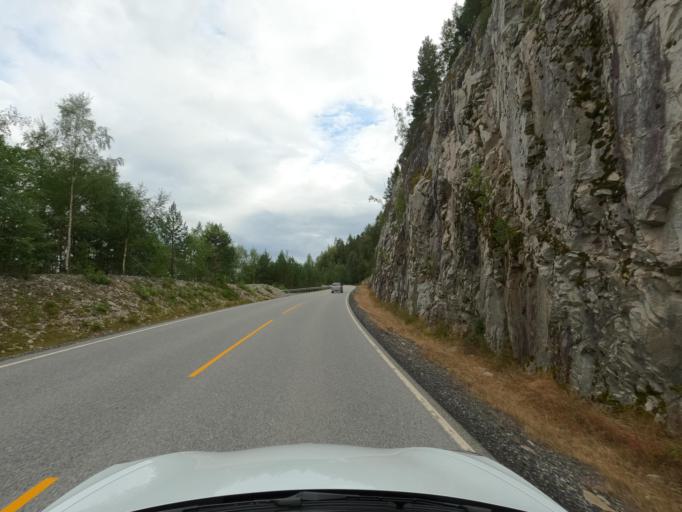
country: NO
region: Telemark
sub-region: Hjartdal
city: Sauland
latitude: 59.7991
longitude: 8.9982
